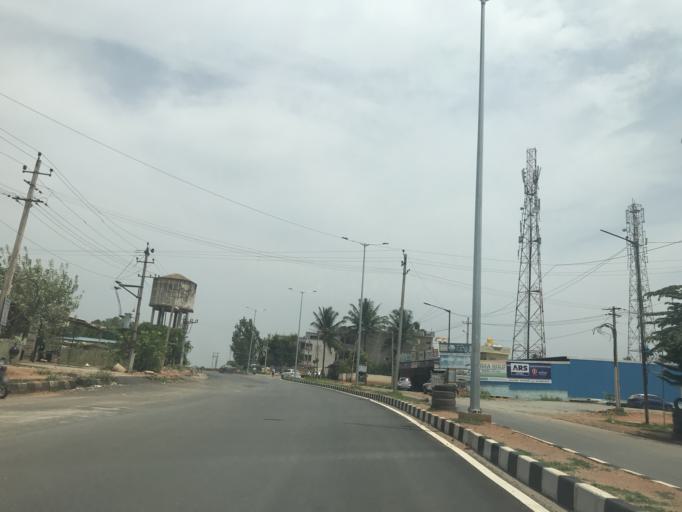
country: IN
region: Karnataka
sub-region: Bangalore Urban
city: Yelahanka
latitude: 13.1312
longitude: 77.6666
